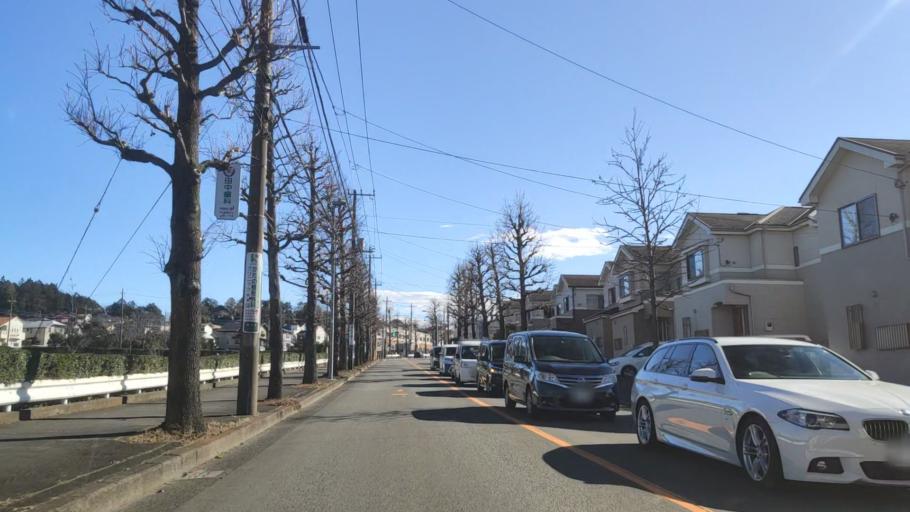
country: JP
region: Tokyo
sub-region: Machida-shi
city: Machida
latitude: 35.5199
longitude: 139.5070
